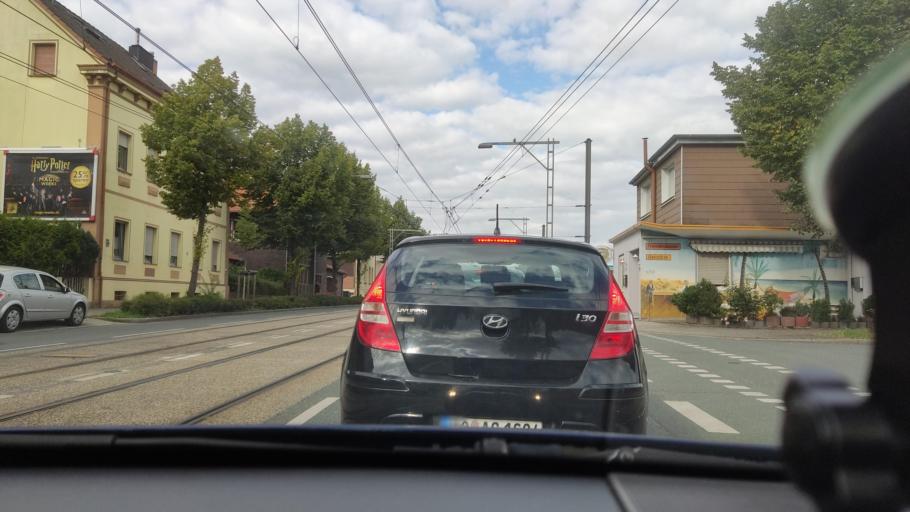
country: DE
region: North Rhine-Westphalia
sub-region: Regierungsbezirk Arnsberg
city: Dortmund
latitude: 51.5417
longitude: 7.4582
